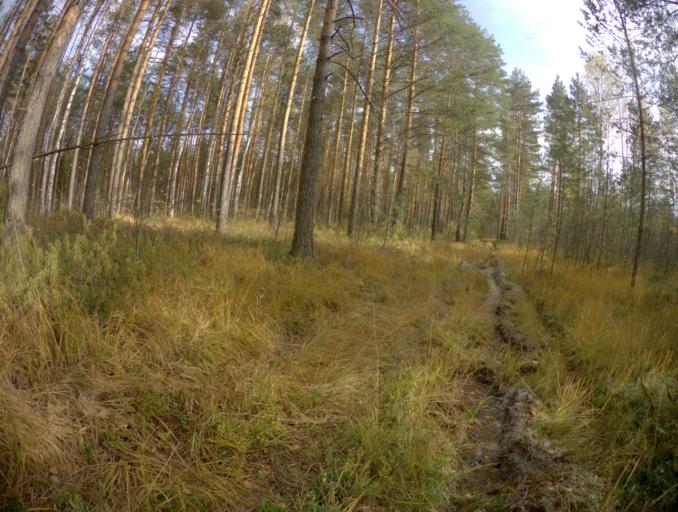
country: RU
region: Vladimir
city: Raduzhnyy
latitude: 55.9389
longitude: 40.3280
